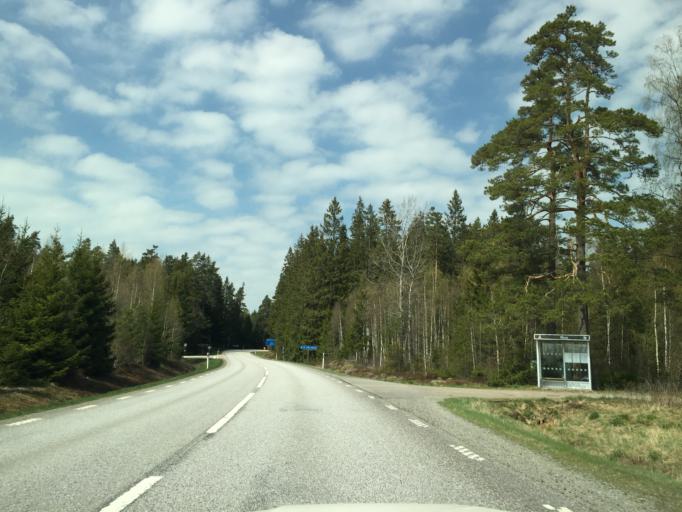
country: SE
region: Vaestra Goetaland
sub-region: Bengtsfors Kommun
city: Dals Langed
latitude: 58.8218
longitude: 12.1400
